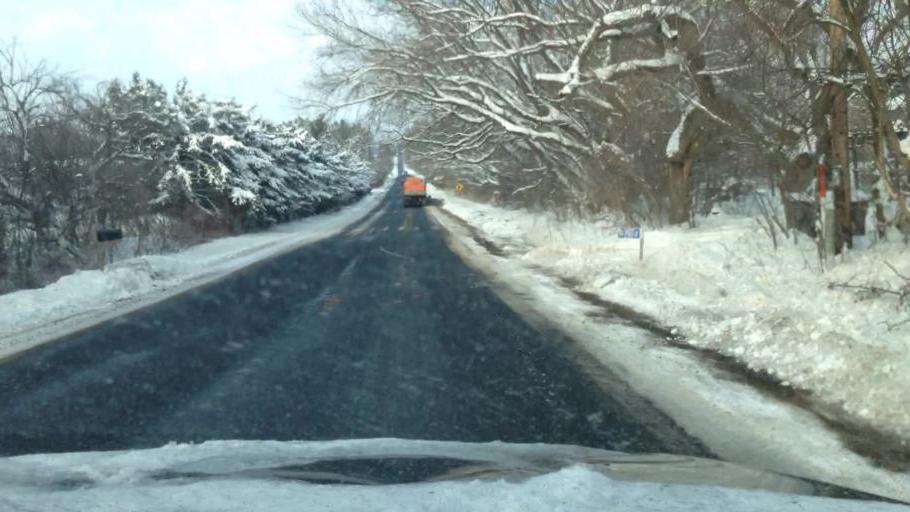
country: US
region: Wisconsin
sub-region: Walworth County
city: East Troy
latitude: 42.7601
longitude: -88.4456
